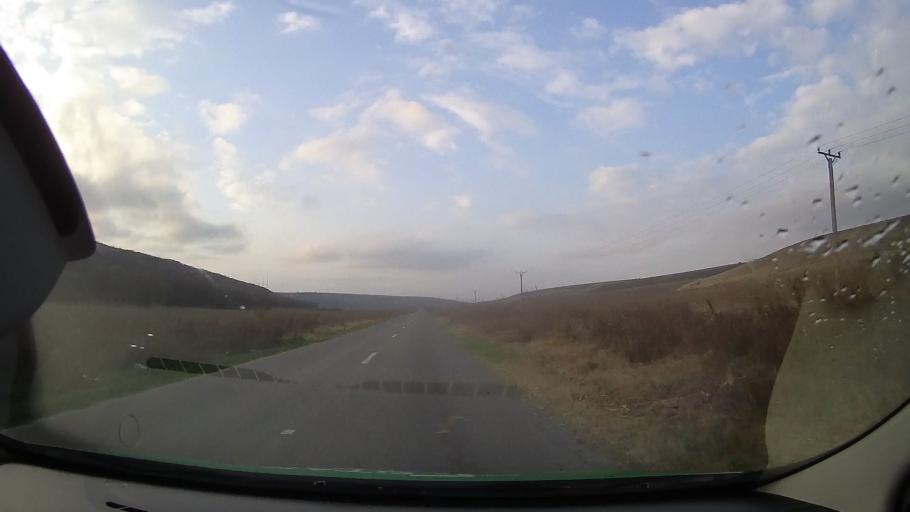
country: RO
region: Constanta
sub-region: Comuna Dobromir
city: Dobromir
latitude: 44.0297
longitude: 27.8607
